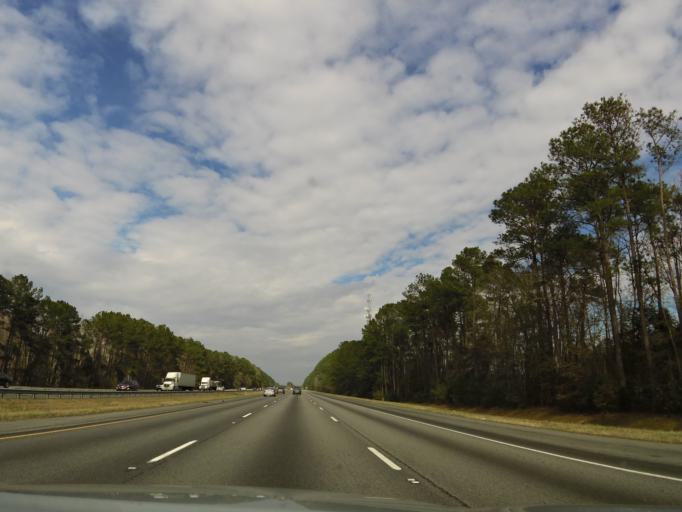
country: US
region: Georgia
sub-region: Bryan County
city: Richmond Hill
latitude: 31.8499
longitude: -81.3439
